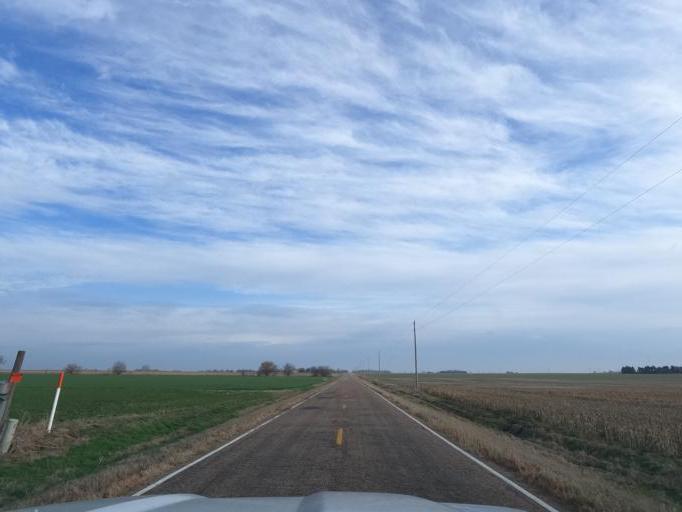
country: US
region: Kansas
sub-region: Rice County
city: Sterling
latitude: 38.0948
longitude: -98.2520
